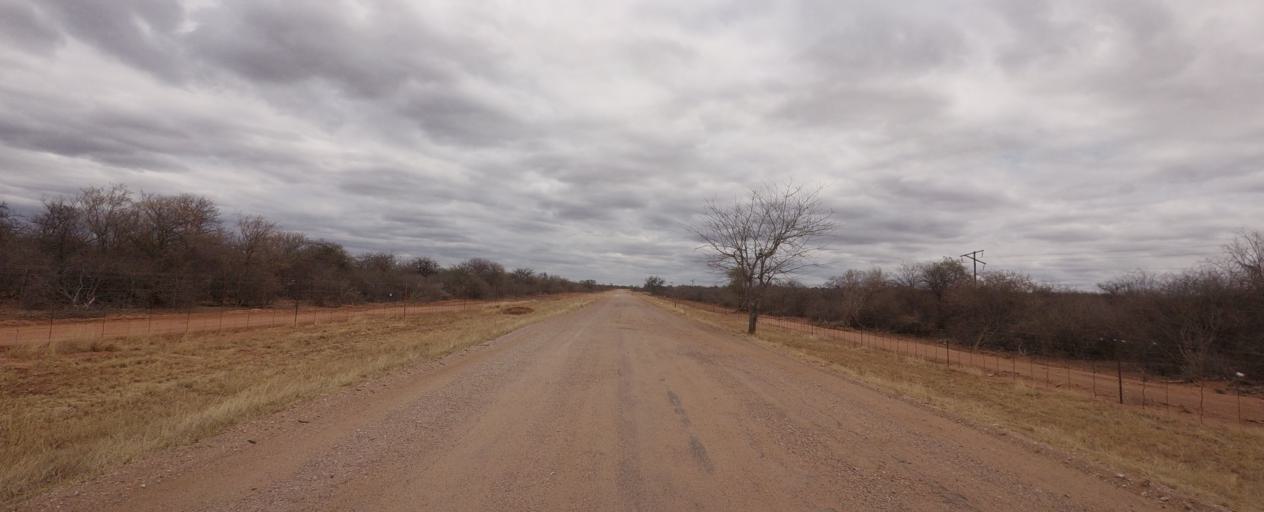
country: BW
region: Central
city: Mathathane
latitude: -22.6985
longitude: 28.6208
